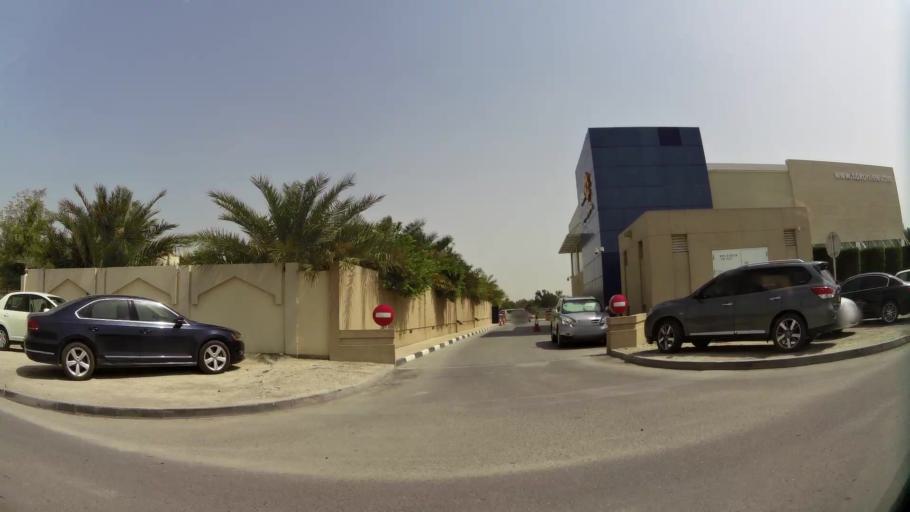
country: BH
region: Manama
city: Jidd Hafs
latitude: 26.2188
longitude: 50.4859
